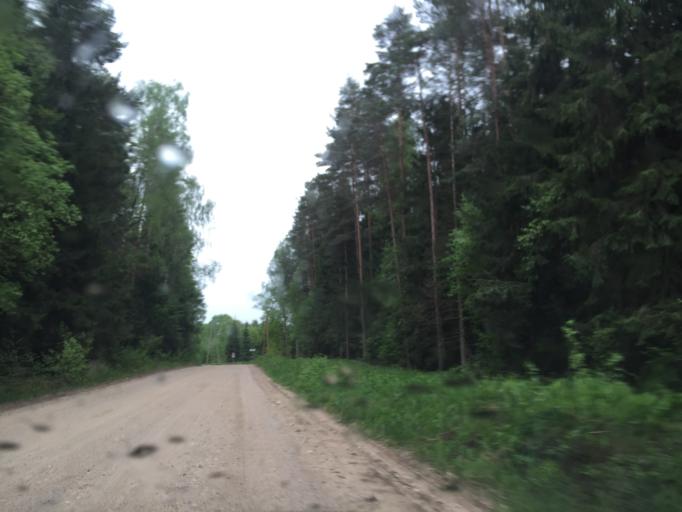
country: LV
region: Ogre
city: Ogre
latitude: 56.8265
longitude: 24.6499
